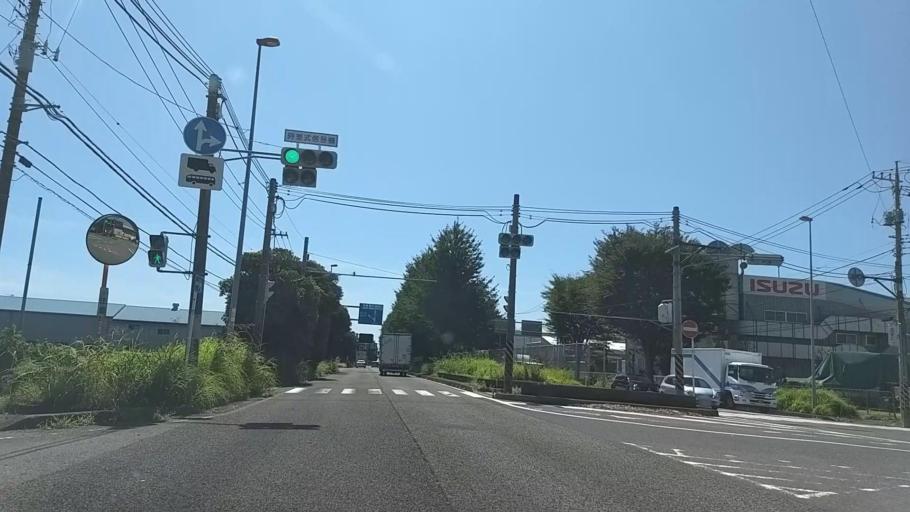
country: JP
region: Kanagawa
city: Zama
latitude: 35.5408
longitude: 139.3612
